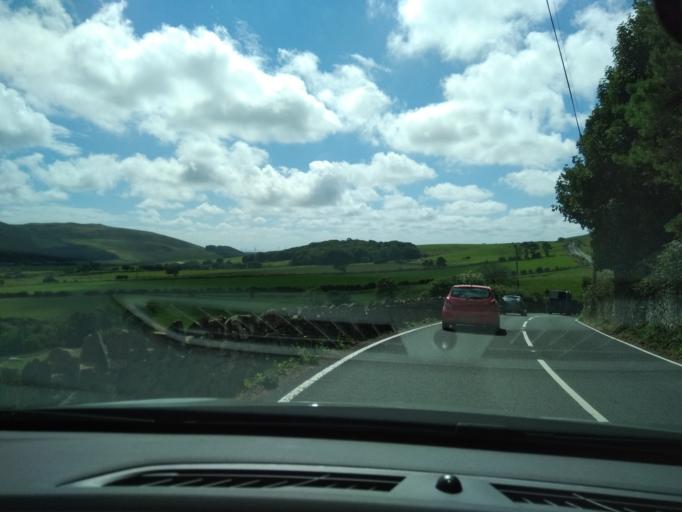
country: GB
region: England
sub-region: Cumbria
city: Millom
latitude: 54.2440
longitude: -3.3143
